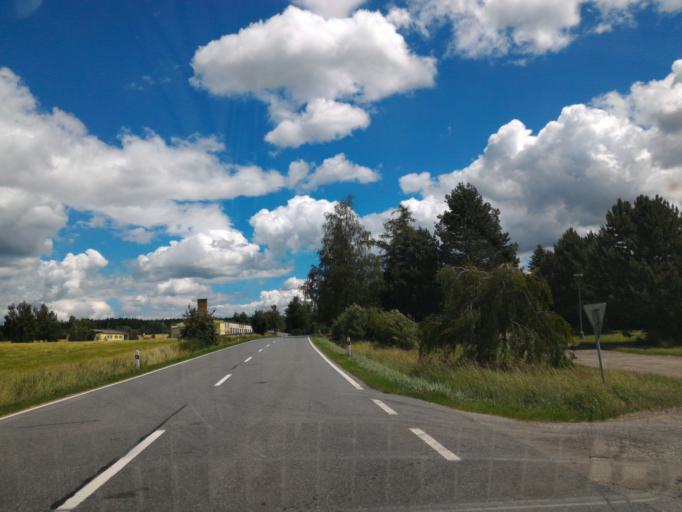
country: CZ
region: Vysocina
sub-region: Okres Jihlava
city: Polna
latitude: 49.4449
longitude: 15.7684
